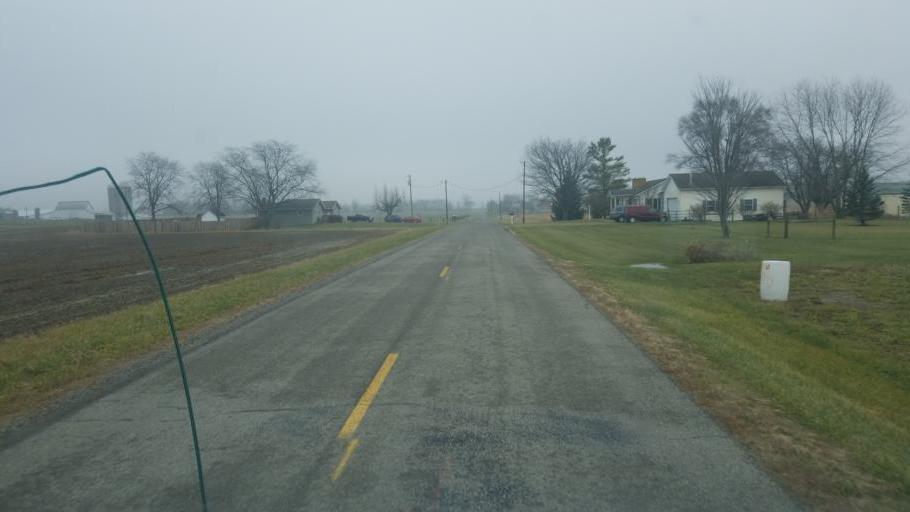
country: US
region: Ohio
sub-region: Champaign County
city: North Lewisburg
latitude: 40.3670
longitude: -83.5455
